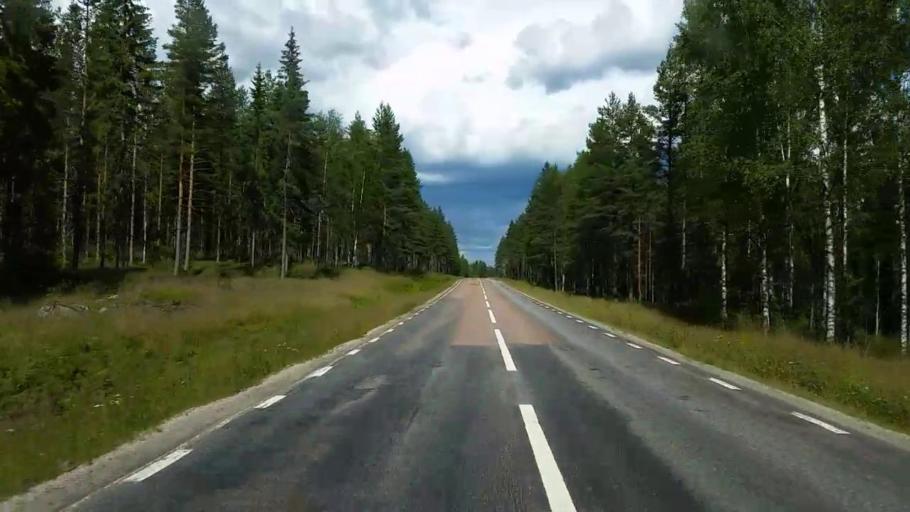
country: SE
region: Gaevleborg
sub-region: Ovanakers Kommun
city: Edsbyn
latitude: 61.3118
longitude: 15.5065
